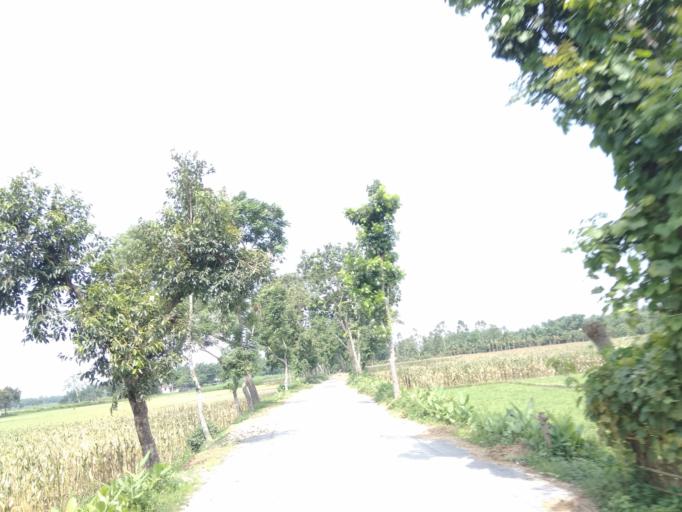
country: BD
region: Rangpur Division
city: Rangpur
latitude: 25.8363
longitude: 89.1995
